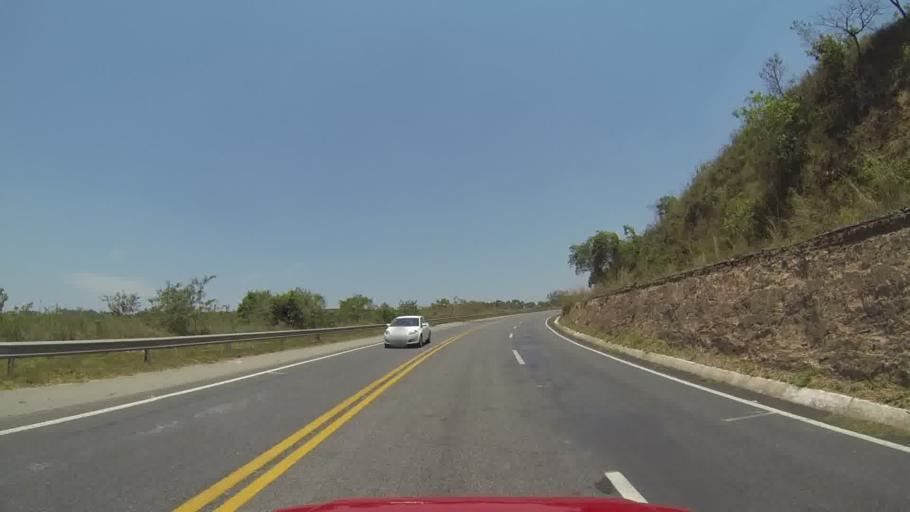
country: BR
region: Minas Gerais
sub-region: Itapecerica
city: Itapecerica
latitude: -20.2874
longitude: -45.1506
